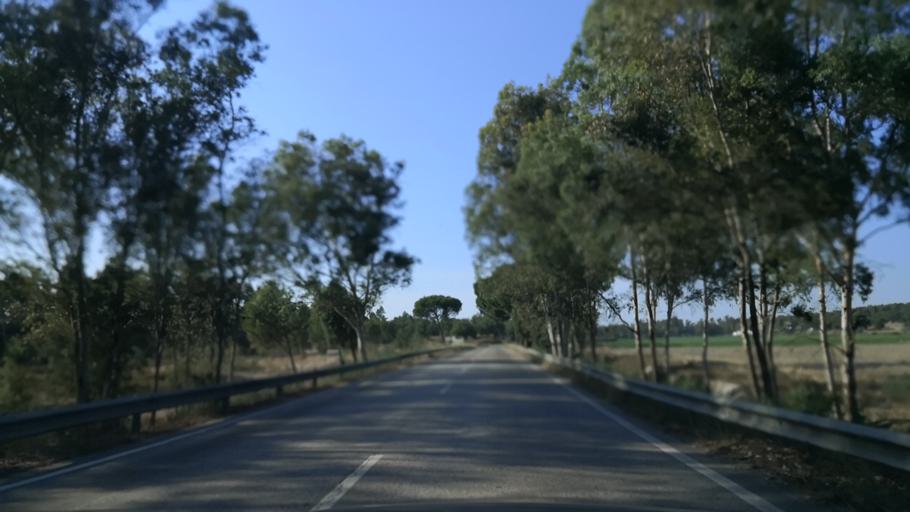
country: PT
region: Santarem
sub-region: Coruche
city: Coruche
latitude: 38.9918
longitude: -8.5538
